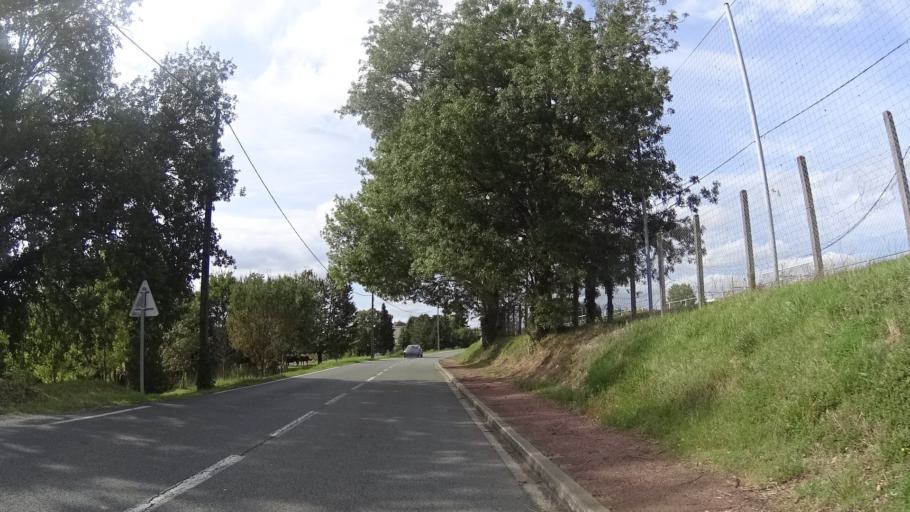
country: FR
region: Aquitaine
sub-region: Departement de la Gironde
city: Lugon-et-l'Ile-du-Carnay
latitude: 44.9897
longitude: -0.3375
